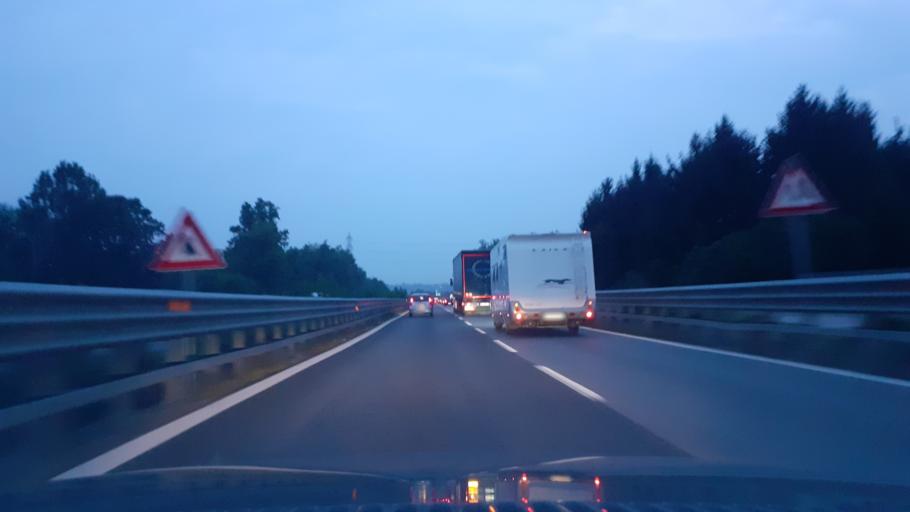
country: IT
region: Lombardy
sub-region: Provincia di Lecco
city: Nibionno
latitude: 45.7425
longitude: 9.2561
